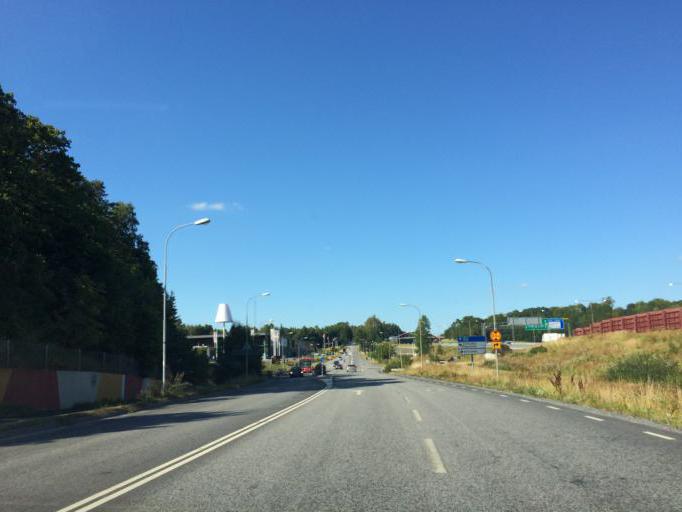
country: SE
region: Stockholm
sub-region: Upplands Vasby Kommun
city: Upplands Vaesby
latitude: 59.4818
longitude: 17.9187
